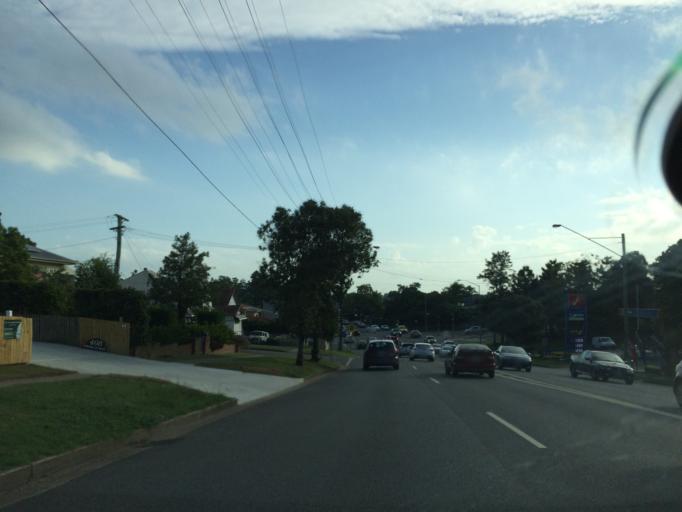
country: AU
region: Queensland
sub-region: Brisbane
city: Taringa
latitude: -27.4990
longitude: 152.9685
